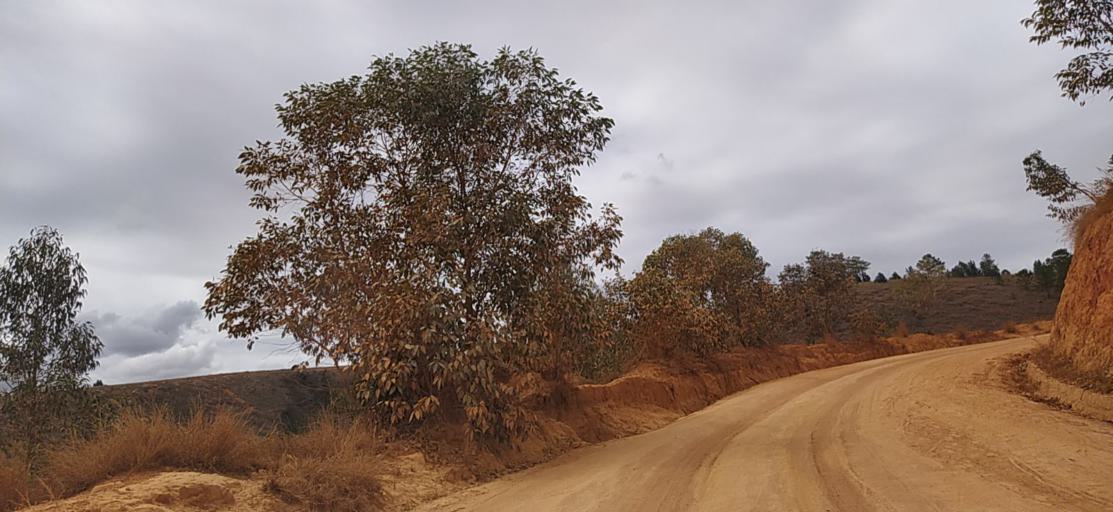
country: MG
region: Alaotra Mangoro
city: Ambatondrazaka
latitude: -17.9971
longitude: 48.2630
